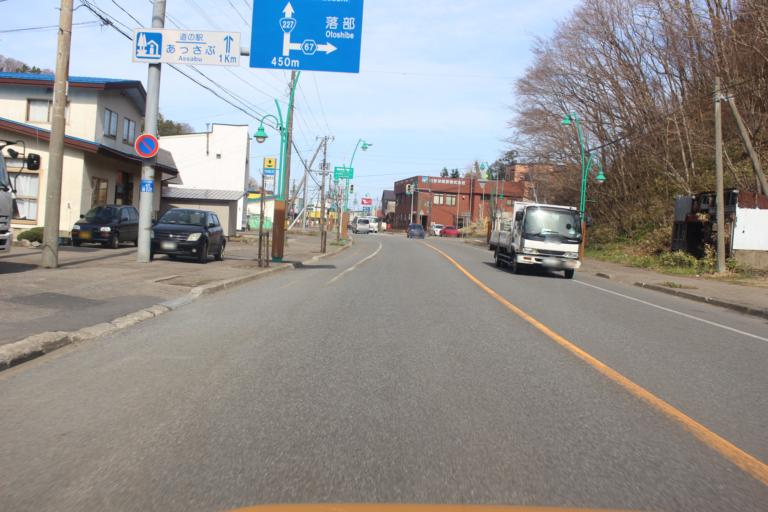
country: JP
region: Hokkaido
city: Kamiiso
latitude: 41.9147
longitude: 140.2276
